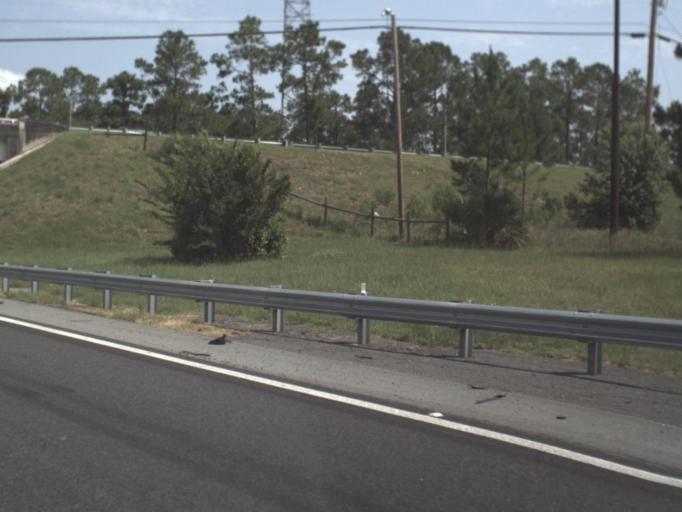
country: US
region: Georgia
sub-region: Echols County
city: Statenville
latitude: 30.5941
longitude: -83.1193
